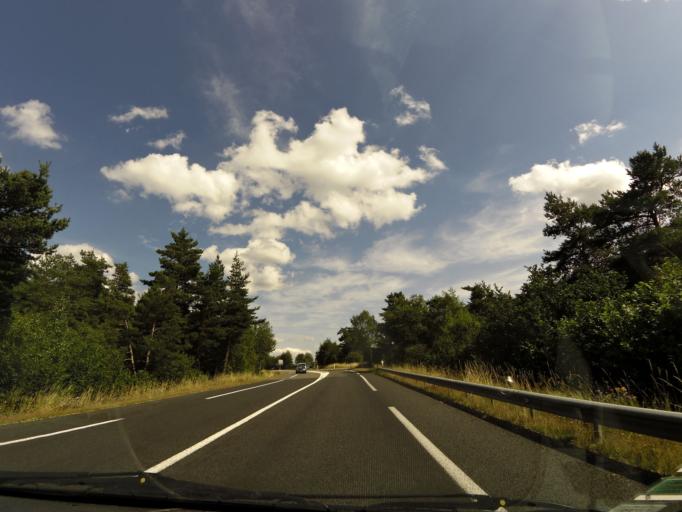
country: FR
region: Auvergne
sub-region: Departement du Puy-de-Dome
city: Aydat
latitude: 45.6828
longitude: 2.9646
